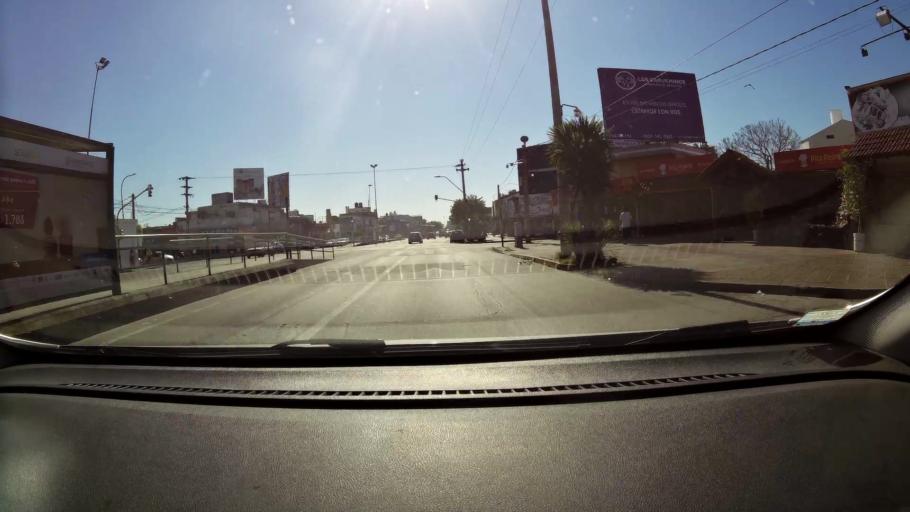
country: AR
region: Cordoba
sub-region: Departamento de Capital
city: Cordoba
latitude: -31.4332
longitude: -64.1523
